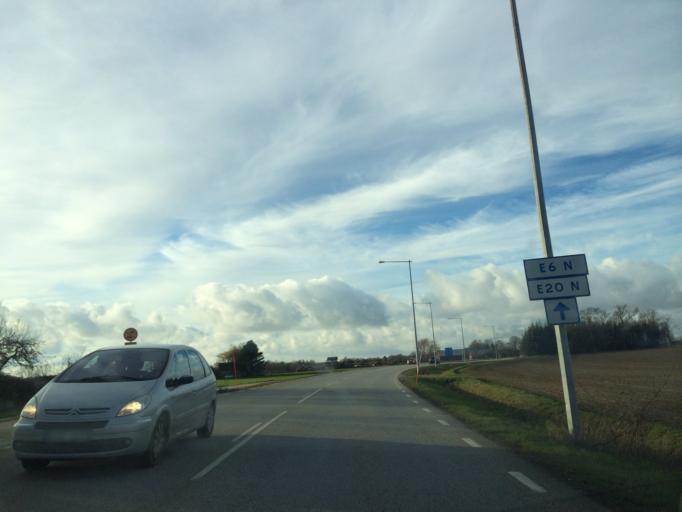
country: SE
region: Skane
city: Bjarred
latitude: 55.7222
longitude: 13.0475
